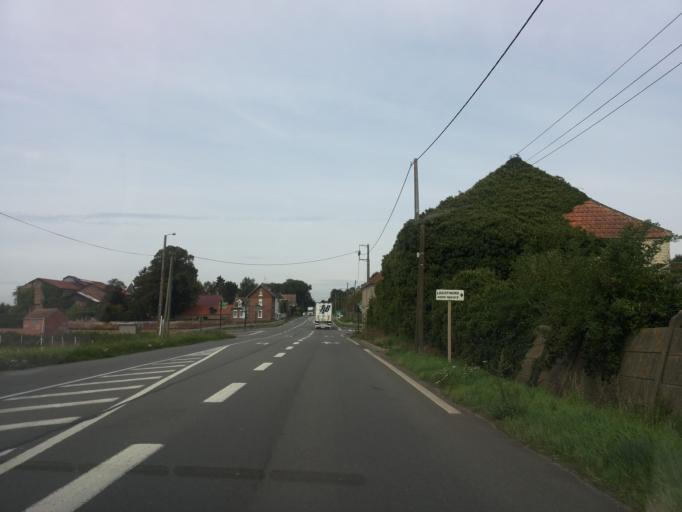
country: FR
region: Nord-Pas-de-Calais
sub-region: Departement du Nord
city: Lecluse
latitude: 50.2280
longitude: 3.0198
